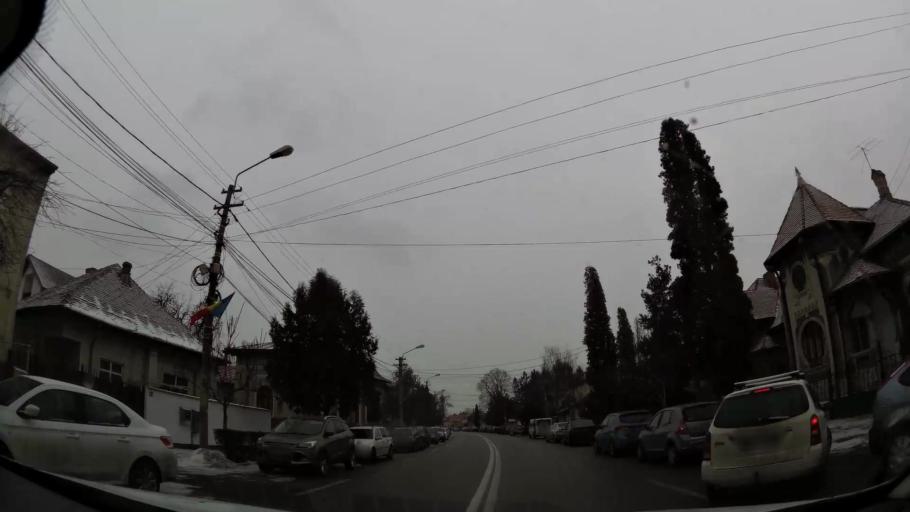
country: RO
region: Dambovita
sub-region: Municipiul Targoviste
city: Targoviste
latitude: 44.9347
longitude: 25.4531
